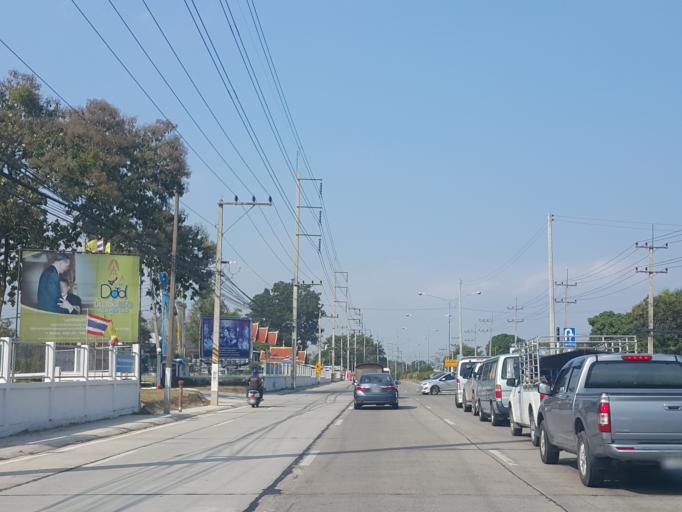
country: TH
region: Chiang Mai
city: San Sai
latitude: 18.8901
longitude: 98.9542
